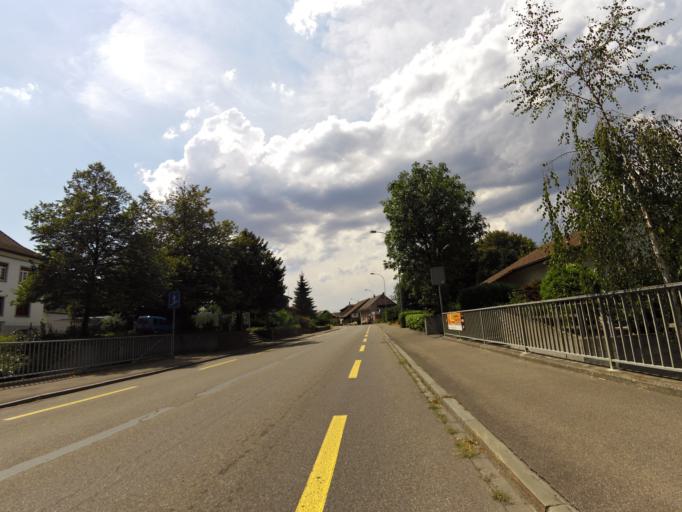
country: CH
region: Aargau
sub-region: Bezirk Lenzburg
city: Othmarsingen
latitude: 47.4121
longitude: 8.2340
